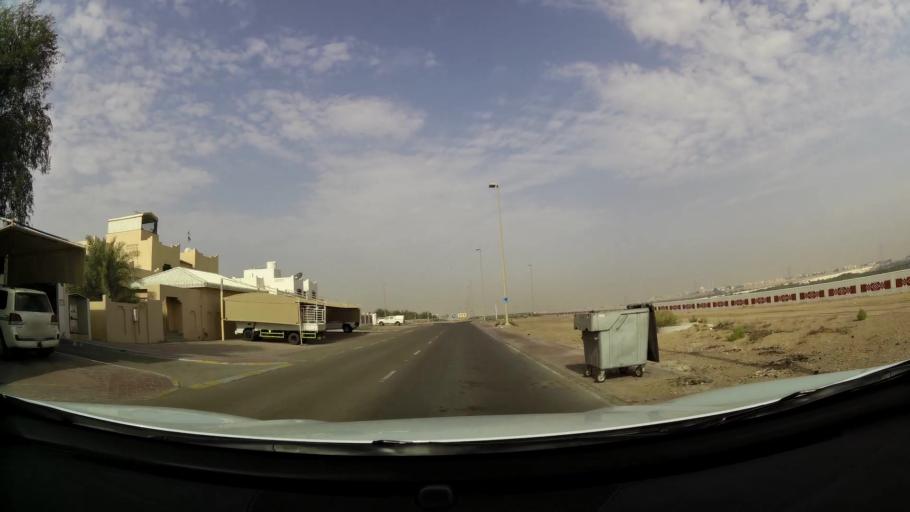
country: AE
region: Abu Dhabi
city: Abu Dhabi
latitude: 24.2447
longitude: 54.7122
